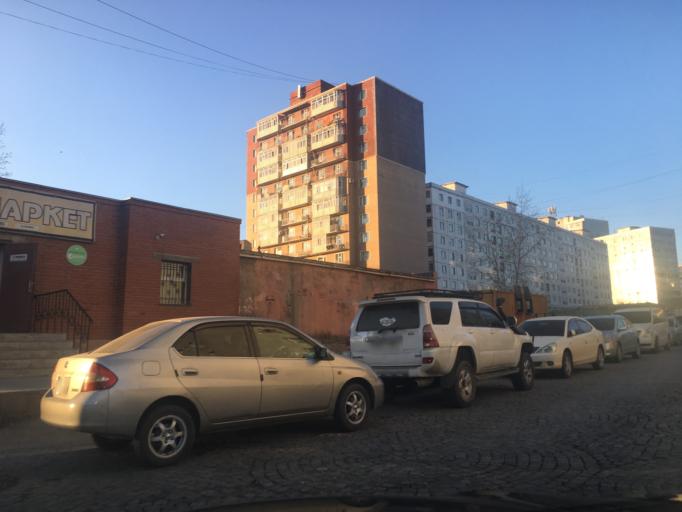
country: MN
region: Ulaanbaatar
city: Ulaanbaatar
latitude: 47.9201
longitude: 106.8812
